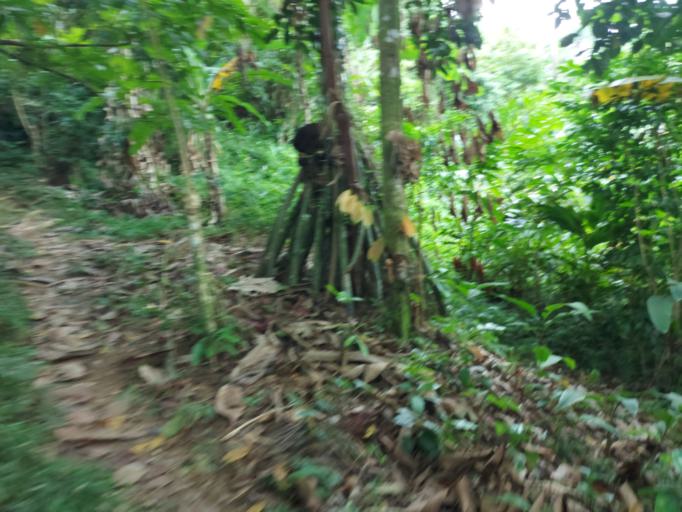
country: PA
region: Bocas del Toro
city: Barranco
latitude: 9.6389
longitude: -82.7822
